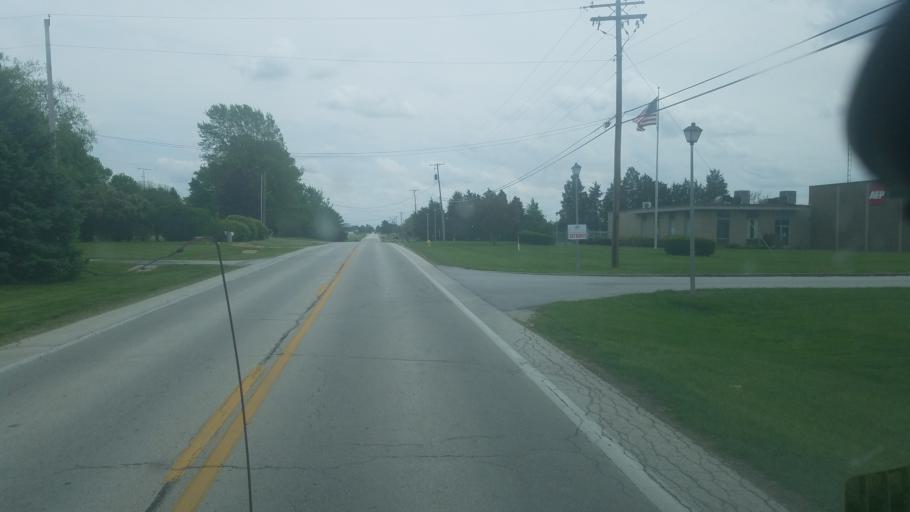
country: US
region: Ohio
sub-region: Seneca County
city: Tiffin
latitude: 41.0863
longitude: -83.1571
